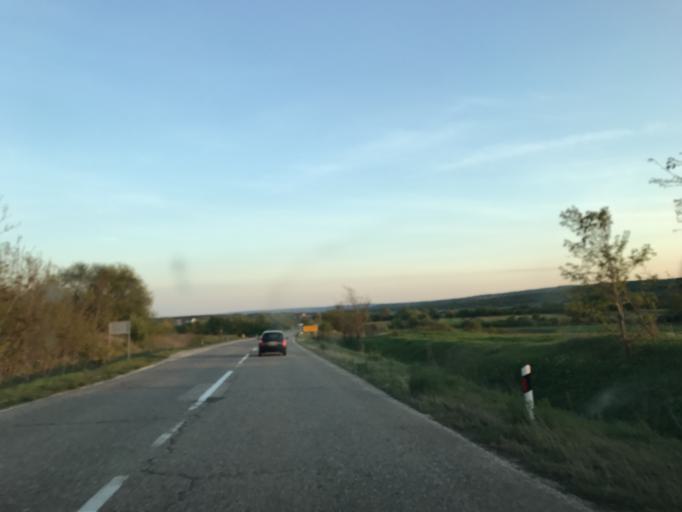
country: RO
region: Mehedinti
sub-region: Comuna Gogosu
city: Ostrovu Mare
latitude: 44.3032
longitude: 22.5067
